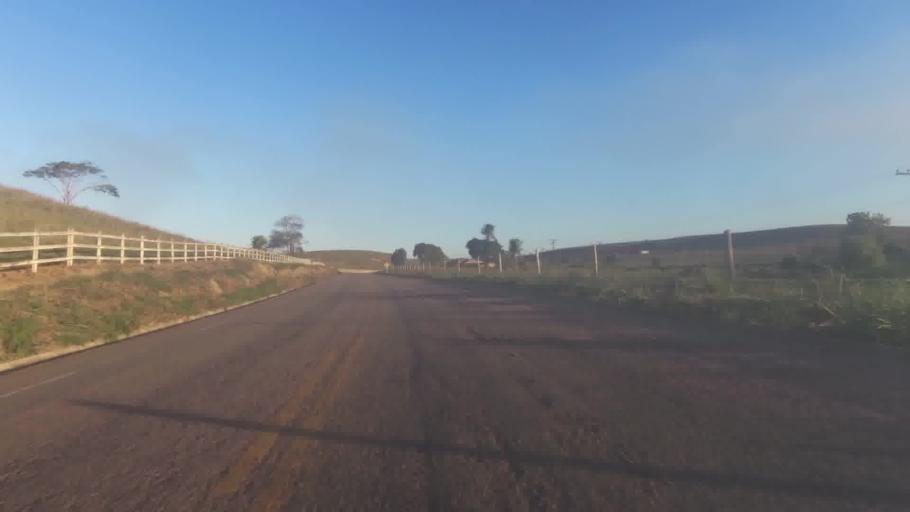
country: BR
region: Espirito Santo
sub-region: Marataizes
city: Marataizes
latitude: -21.1531
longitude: -40.9981
